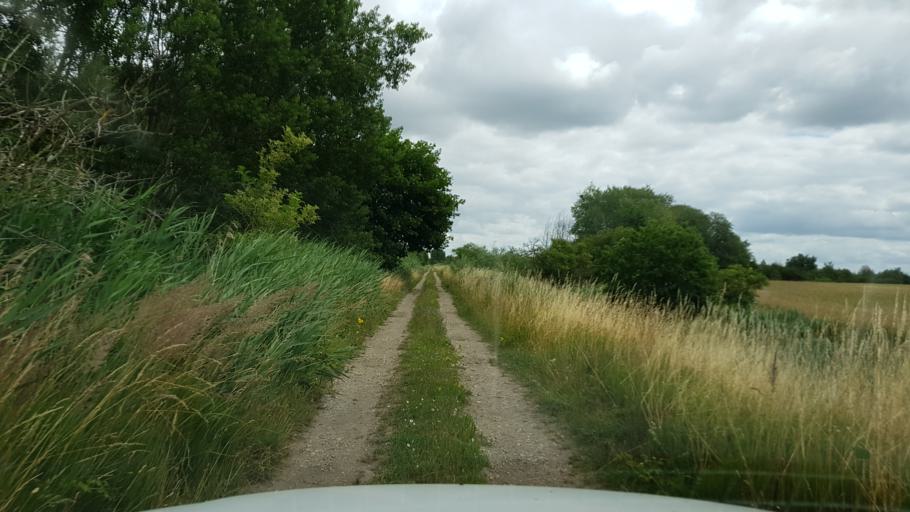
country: PL
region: West Pomeranian Voivodeship
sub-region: Powiat mysliborski
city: Mysliborz
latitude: 52.9423
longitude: 14.9262
